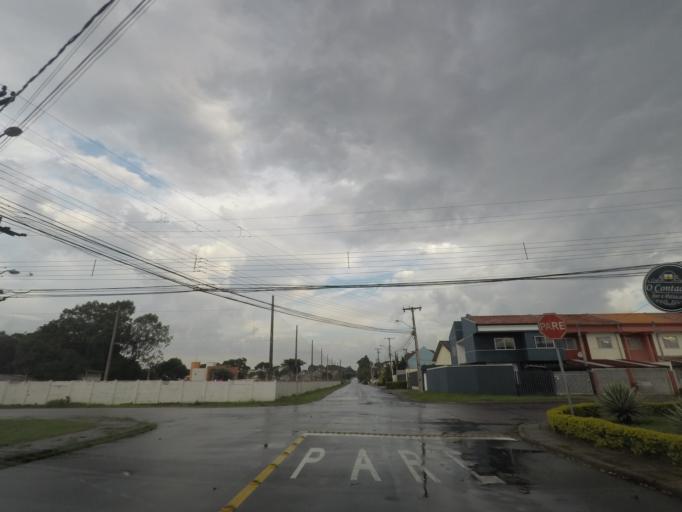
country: BR
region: Parana
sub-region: Sao Jose Dos Pinhais
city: Sao Jose dos Pinhais
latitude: -25.4919
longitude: -49.2477
